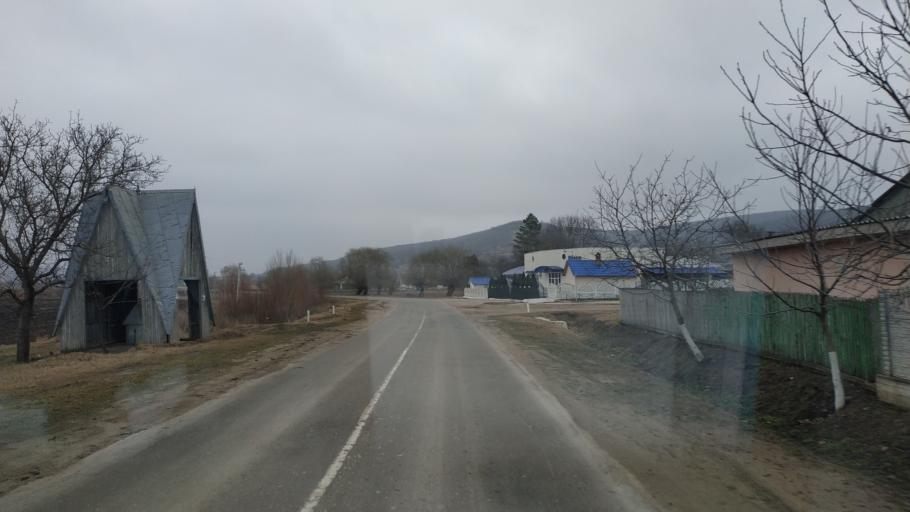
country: MD
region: Hincesti
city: Hincesti
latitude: 46.9597
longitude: 28.4864
